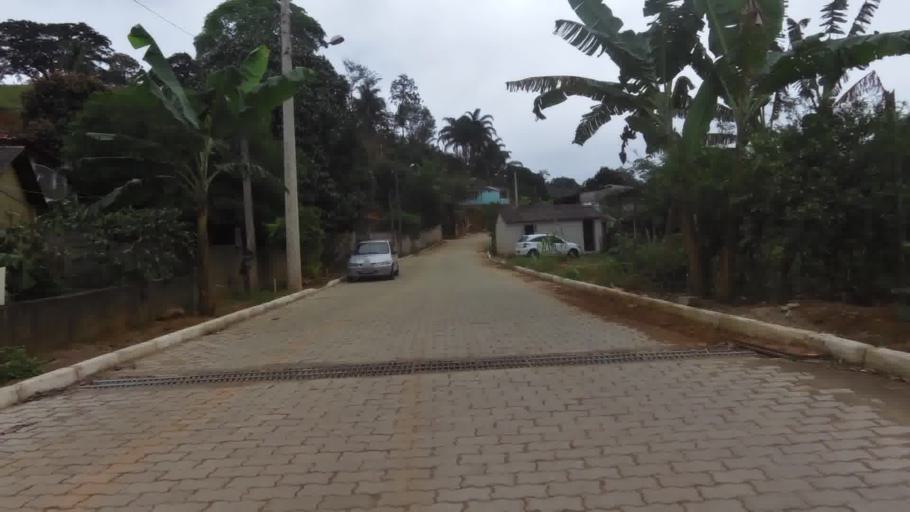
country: BR
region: Espirito Santo
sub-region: Iconha
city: Iconha
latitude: -20.7860
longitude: -40.8243
